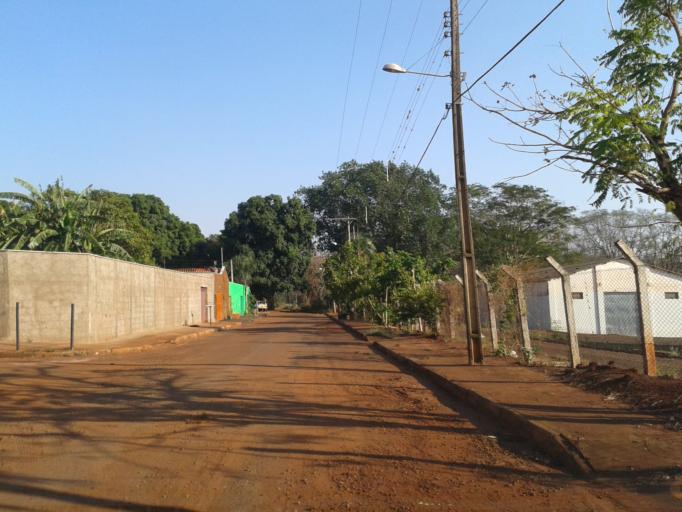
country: BR
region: Minas Gerais
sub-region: Ituiutaba
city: Ituiutaba
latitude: -18.9466
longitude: -49.4597
